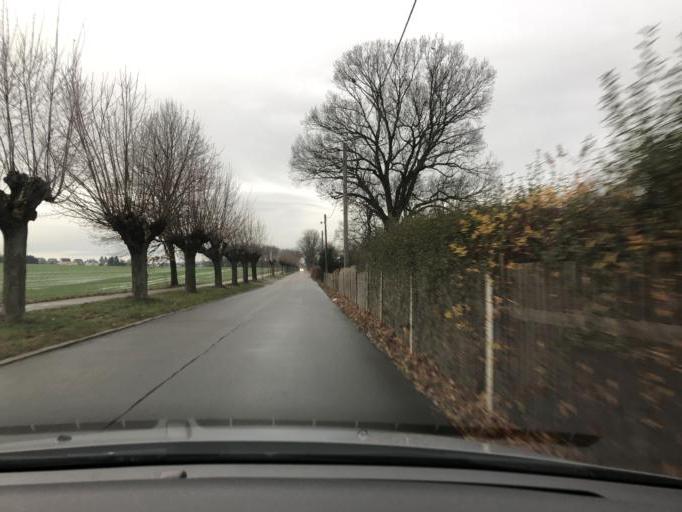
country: DE
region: Saxony
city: Limbach-Oberfrohna
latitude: 50.8609
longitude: 12.7313
